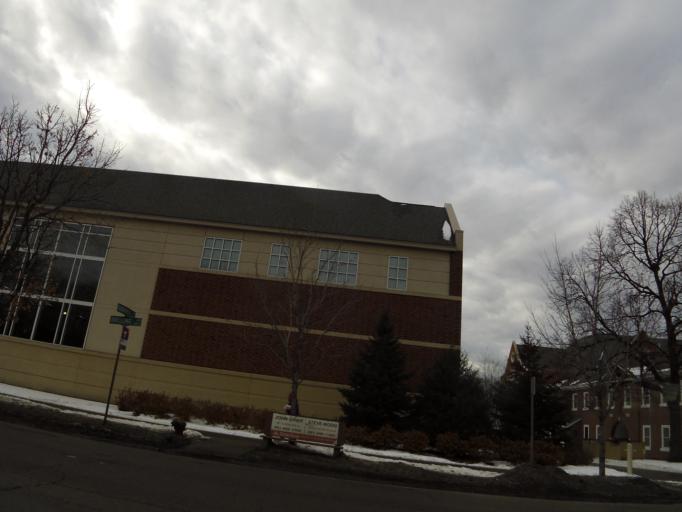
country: US
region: Minnesota
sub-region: Ramsey County
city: Falcon Heights
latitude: 44.9380
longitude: -93.1672
